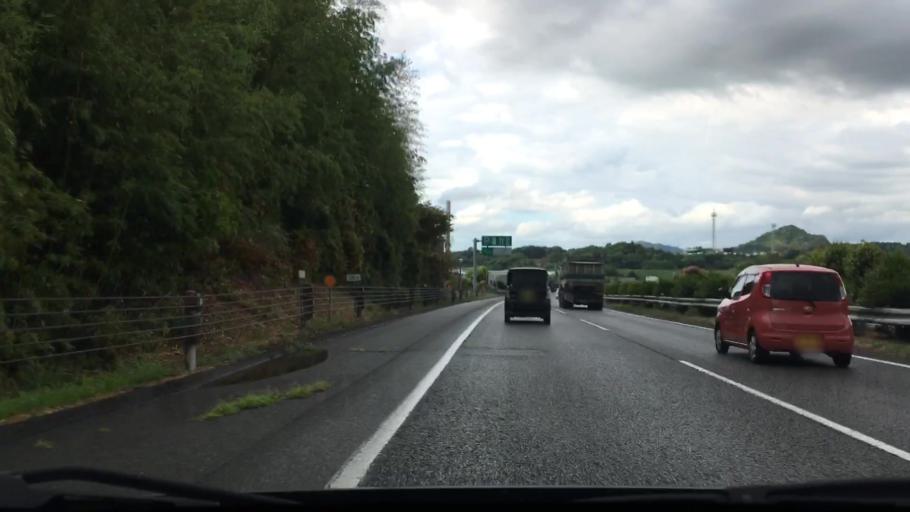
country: JP
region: Fukuoka
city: Koga
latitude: 33.7274
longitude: 130.5038
